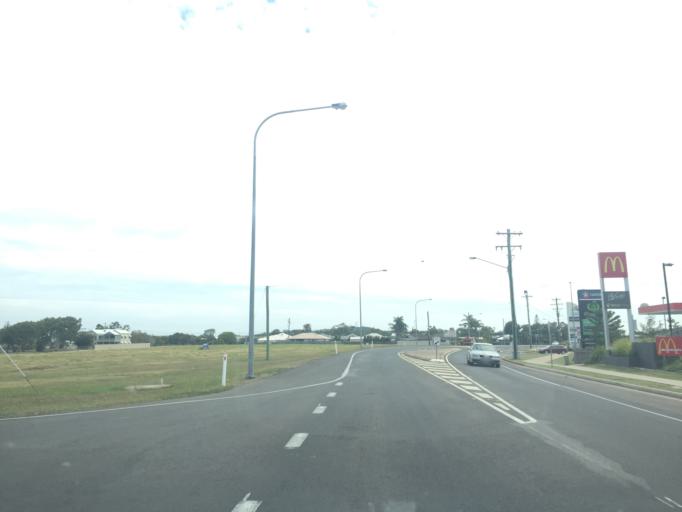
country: AU
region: Queensland
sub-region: Bundaberg
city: Bundaberg
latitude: -24.8185
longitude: 152.4578
